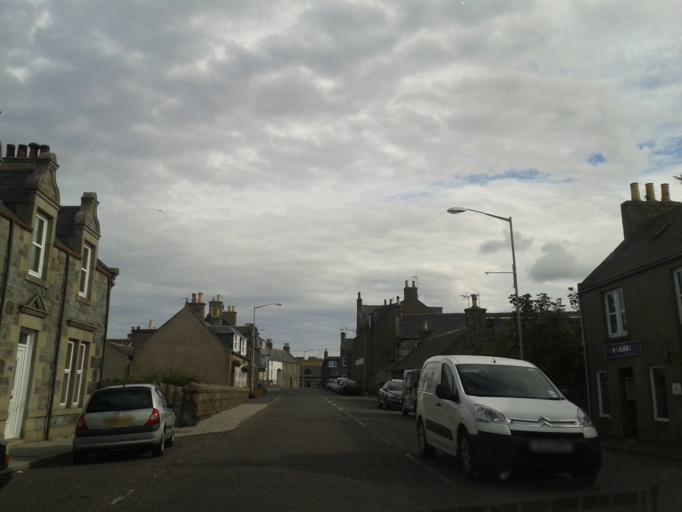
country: GB
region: Scotland
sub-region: Aberdeenshire
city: Portsoy
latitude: 57.6815
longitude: -2.6897
